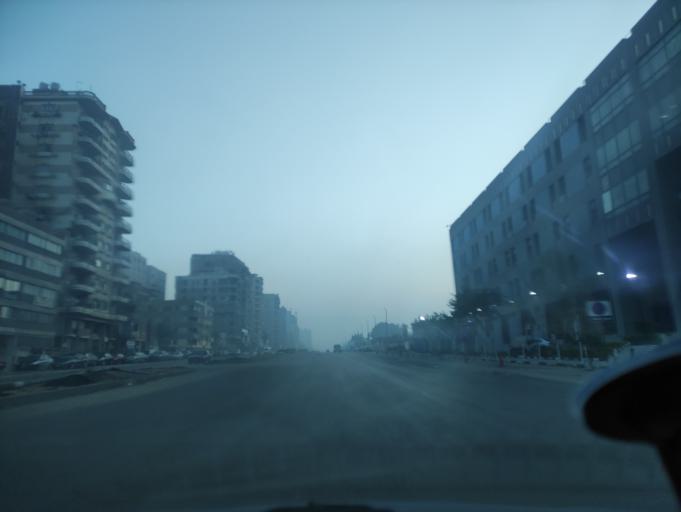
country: EG
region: Muhafazat al Qahirah
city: Cairo
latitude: 30.0450
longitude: 31.3424
